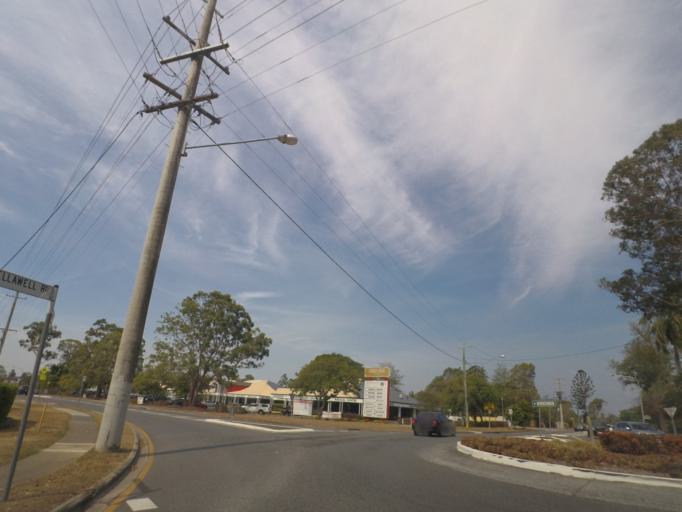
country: AU
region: Queensland
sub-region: Brisbane
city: Sunnybank
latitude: -27.5974
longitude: 153.0440
